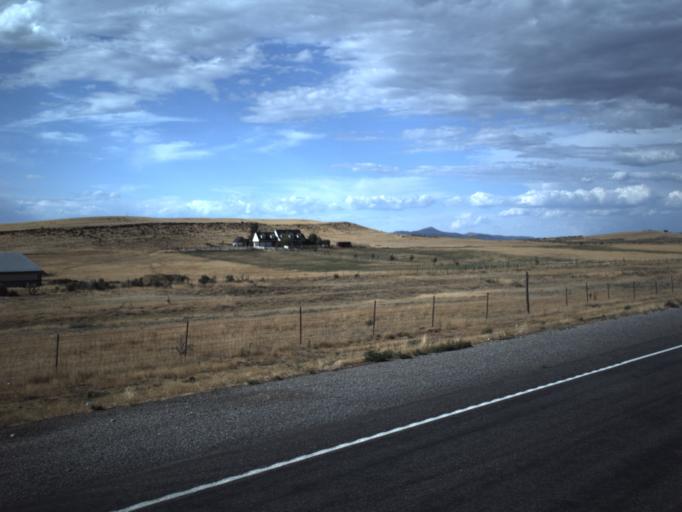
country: US
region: Utah
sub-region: Sanpete County
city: Ephraim
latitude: 39.4028
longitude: -111.5682
